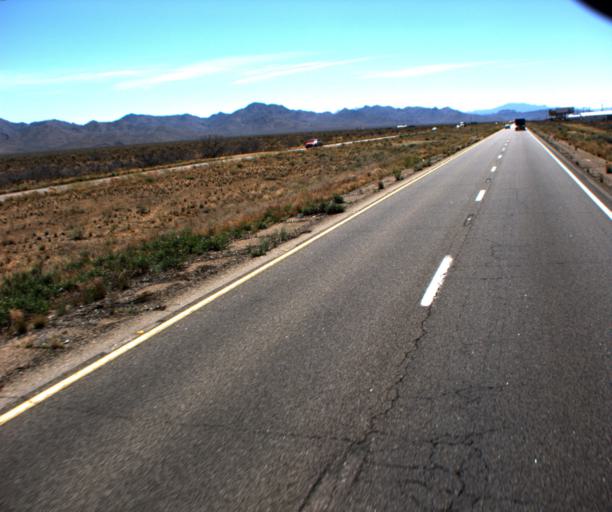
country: US
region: Arizona
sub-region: Mohave County
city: Golden Valley
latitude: 35.3411
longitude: -114.2193
